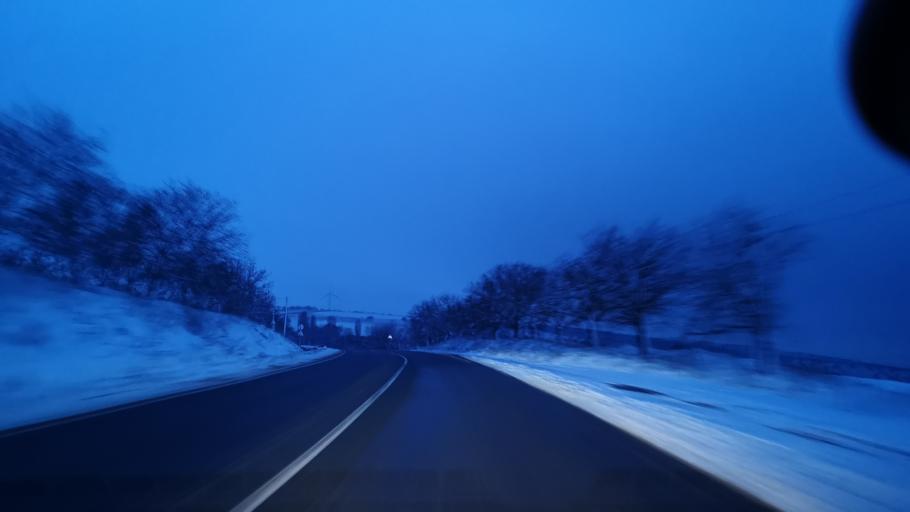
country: MD
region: Rezina
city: Saharna
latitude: 47.5952
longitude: 28.8244
